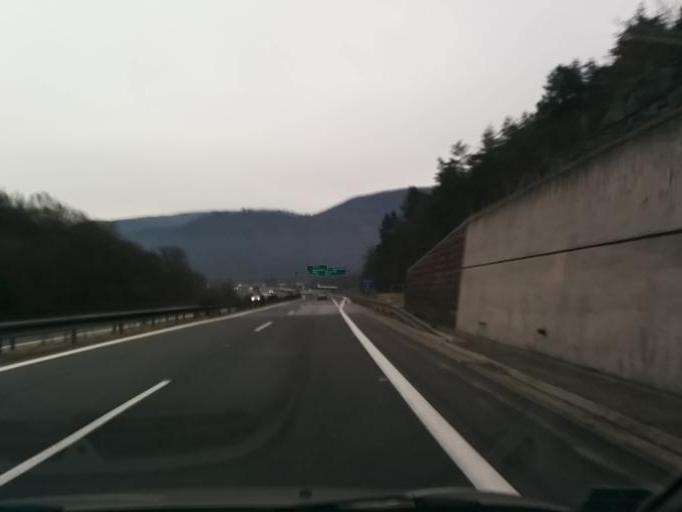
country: SK
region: Nitriansky
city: Tlmace
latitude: 48.3632
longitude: 18.5701
